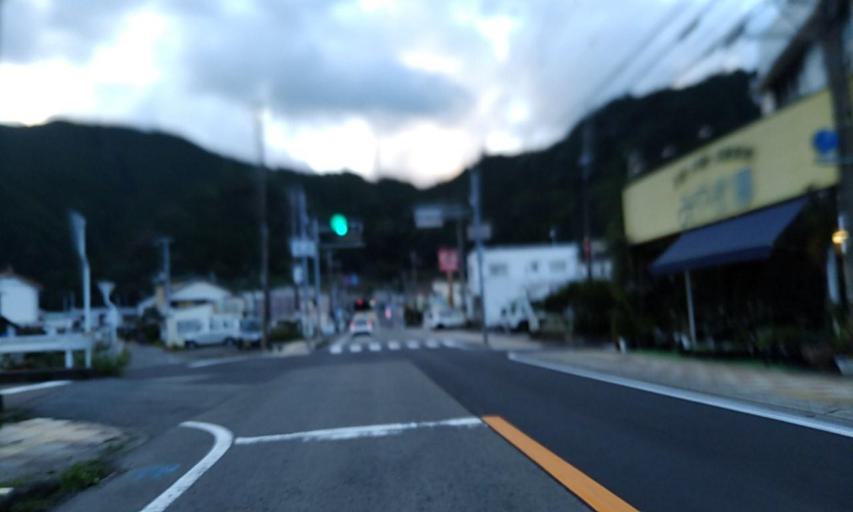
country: JP
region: Wakayama
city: Shingu
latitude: 33.7190
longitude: 135.9834
